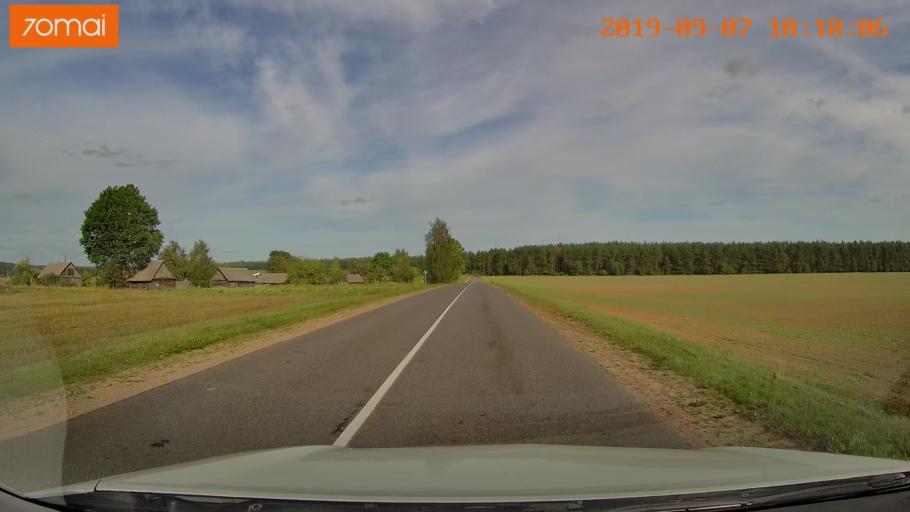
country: BY
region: Grodnenskaya
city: Voranava
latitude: 54.1040
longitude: 25.3703
